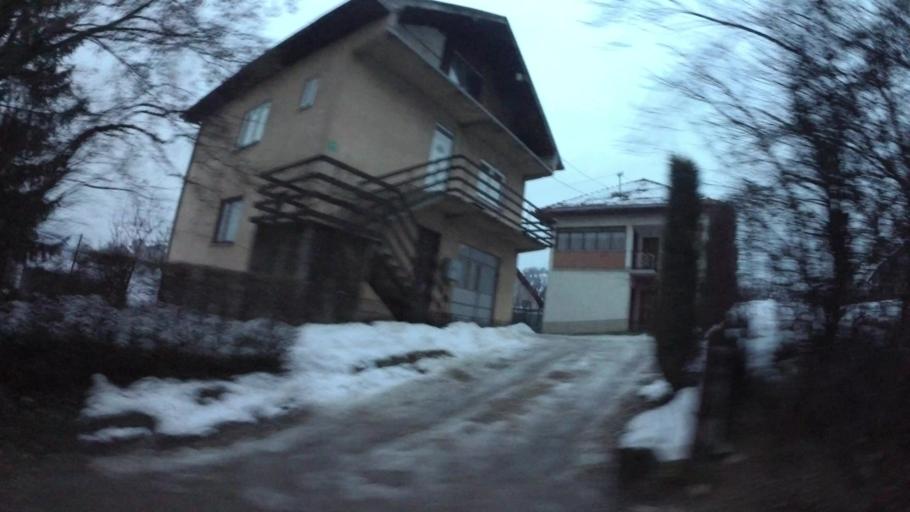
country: BA
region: Federation of Bosnia and Herzegovina
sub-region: Kanton Sarajevo
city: Sarajevo
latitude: 43.8534
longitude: 18.3407
